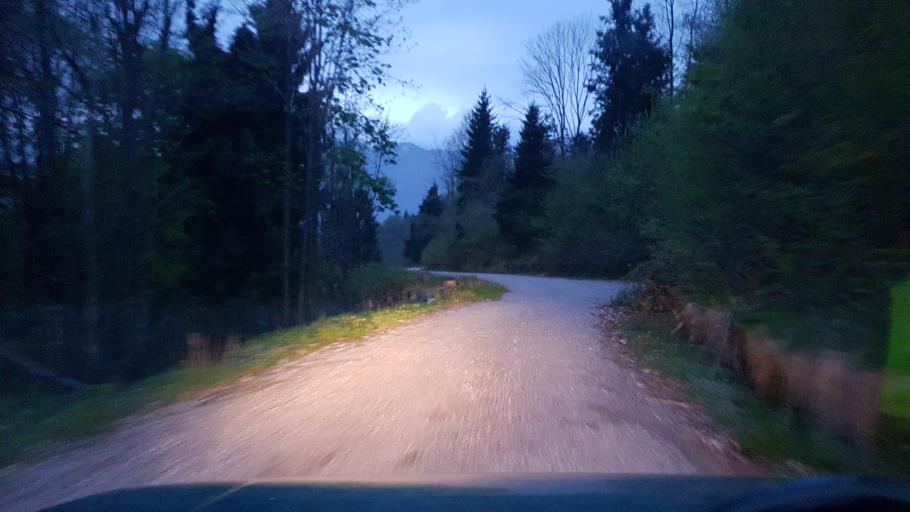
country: IT
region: Friuli Venezia Giulia
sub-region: Provincia di Udine
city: Taipana
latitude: 46.2350
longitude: 13.3542
